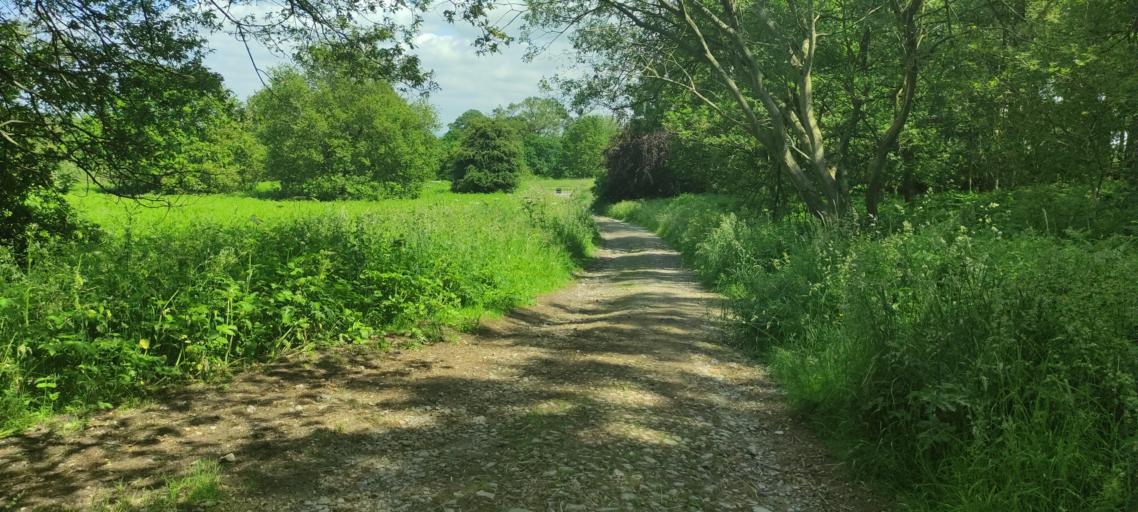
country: GB
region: England
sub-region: North Yorkshire
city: Bedale
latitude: 54.1992
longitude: -1.6598
